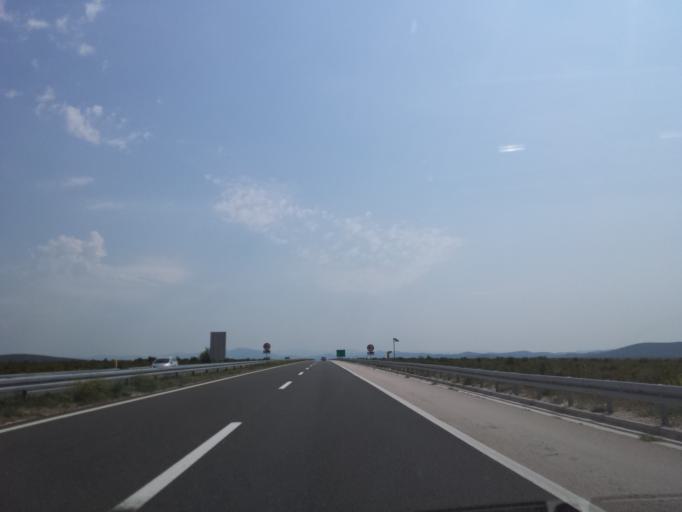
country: HR
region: Sibensko-Kniniska
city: Zaton
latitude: 43.8835
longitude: 15.7949
